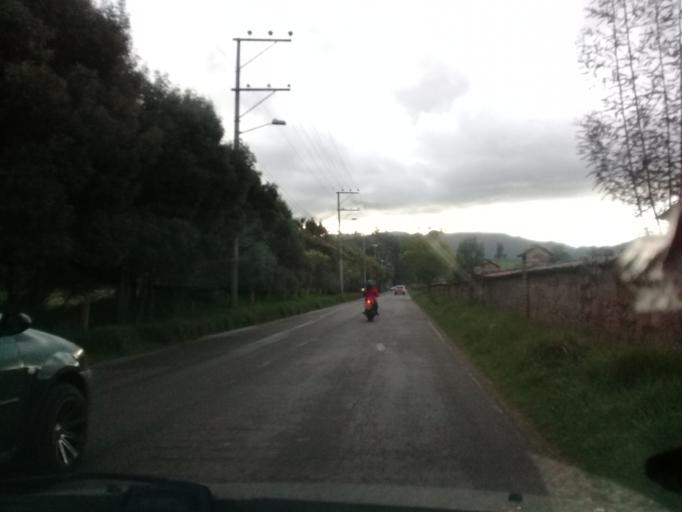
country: CO
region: Cundinamarca
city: Tabio
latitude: 4.9260
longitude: -74.0695
